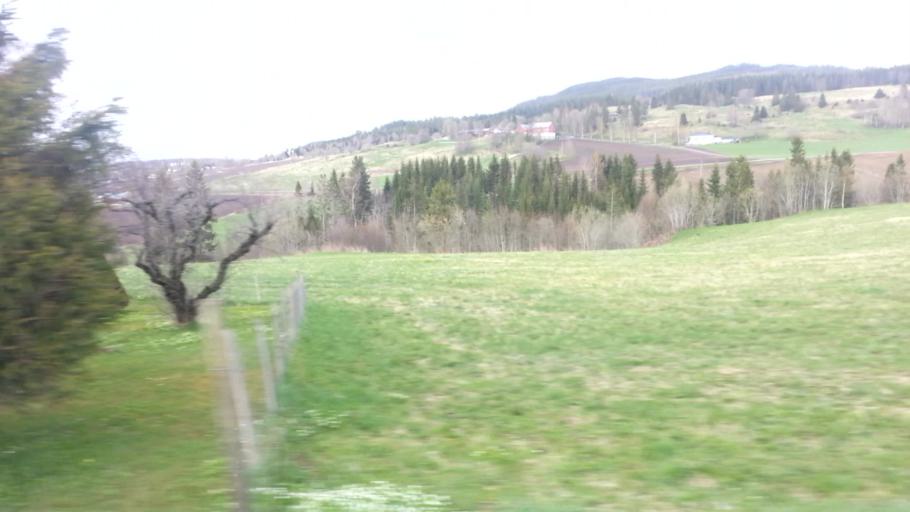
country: NO
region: Nord-Trondelag
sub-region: Levanger
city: Skogn
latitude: 63.6597
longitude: 11.2321
